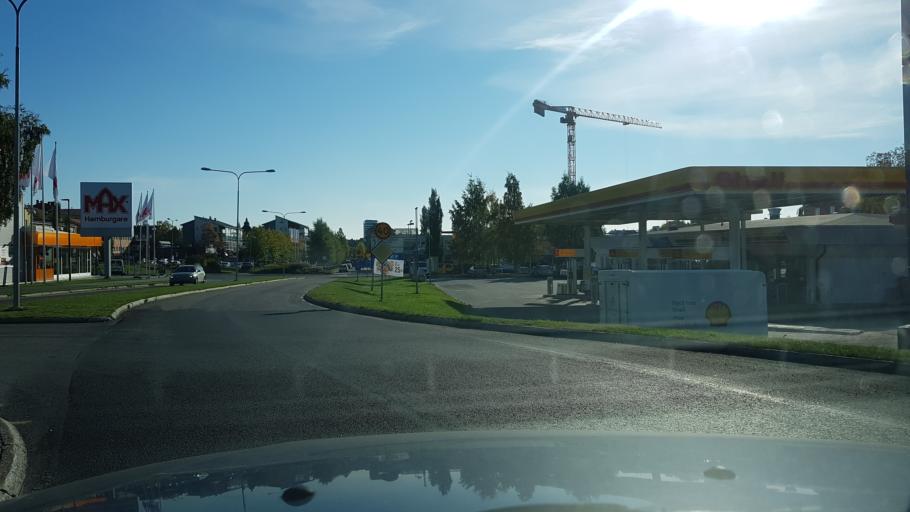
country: SE
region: Norrbotten
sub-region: Pitea Kommun
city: Pitea
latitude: 65.3209
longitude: 21.4724
